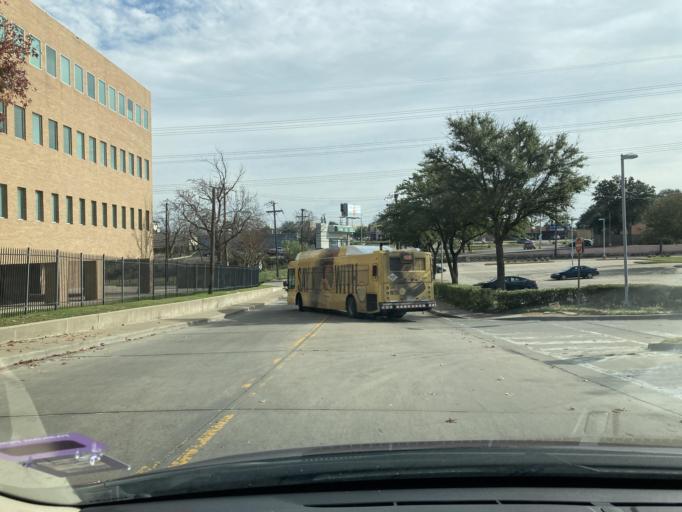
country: US
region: Texas
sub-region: Dallas County
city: University Park
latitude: 32.8734
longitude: -96.7655
